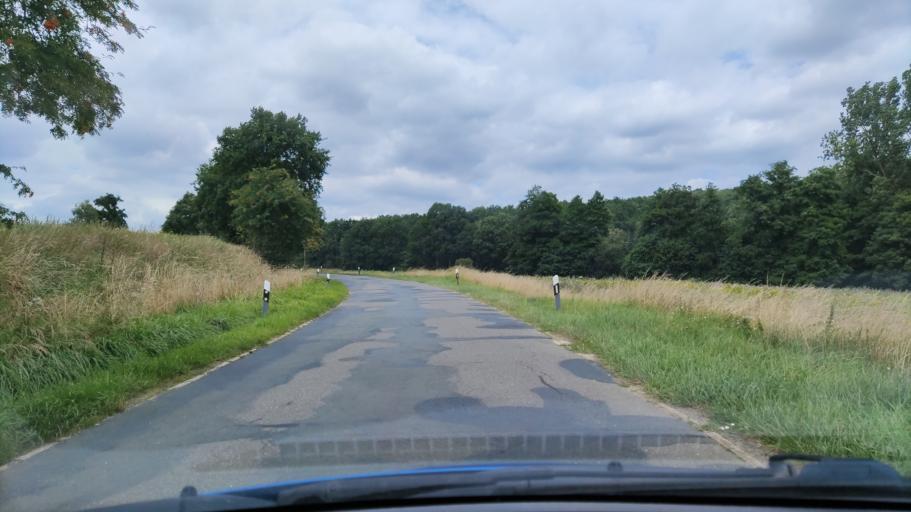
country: DE
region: Lower Saxony
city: Weste
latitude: 53.0787
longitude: 10.6892
